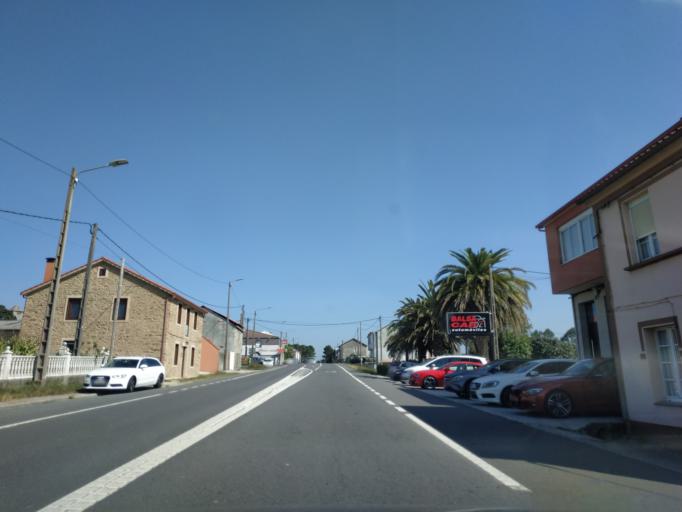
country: ES
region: Galicia
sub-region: Provincia da Coruna
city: Carballo
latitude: 43.2301
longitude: -8.6659
